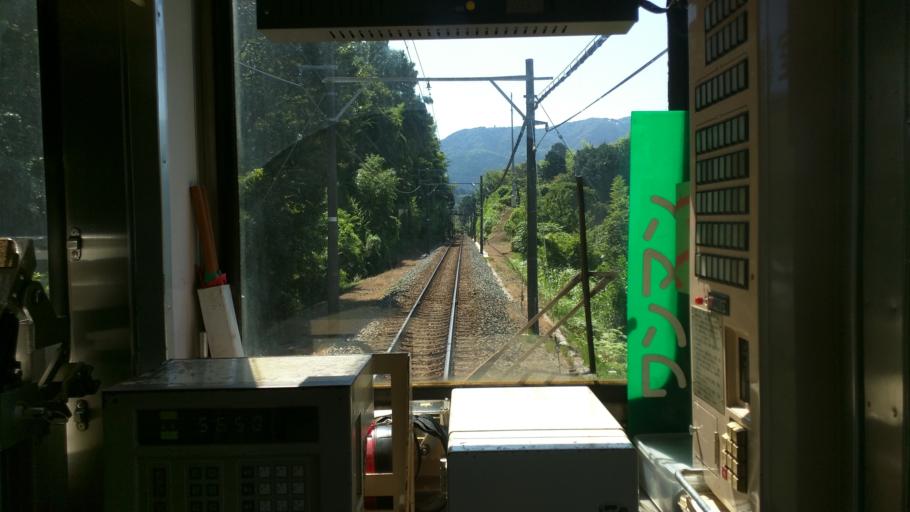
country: JP
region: Shizuoka
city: Ito
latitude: 34.9509
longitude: 139.1014
